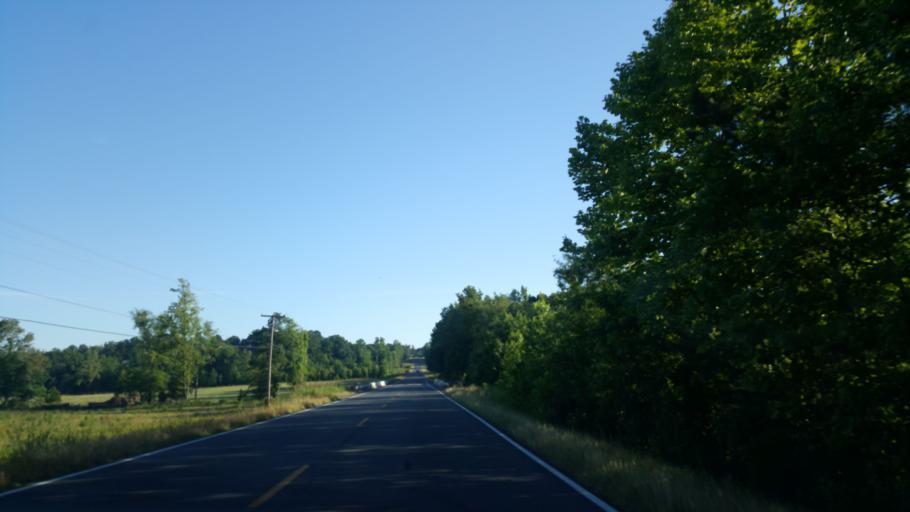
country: US
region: Tennessee
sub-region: Henderson County
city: Lexington
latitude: 35.5794
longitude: -88.3889
